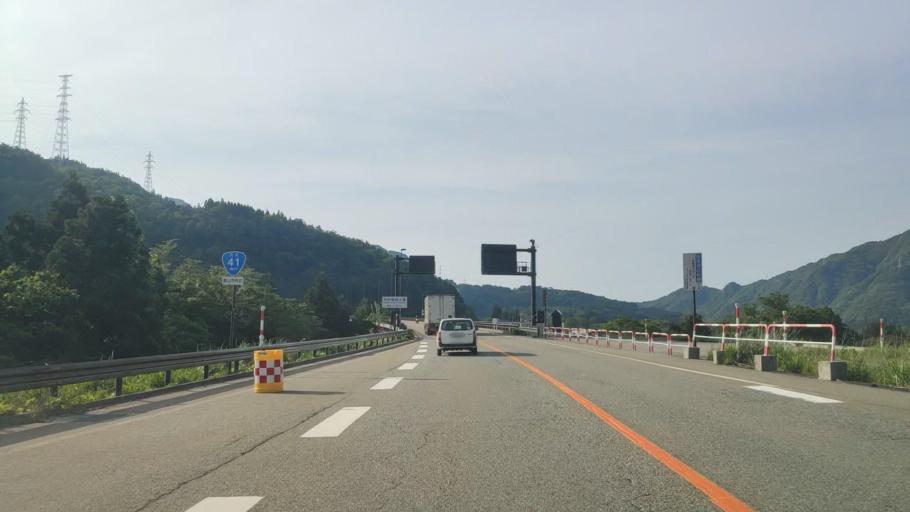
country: JP
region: Toyama
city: Yatsuomachi-higashikumisaka
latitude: 36.5246
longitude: 137.2306
